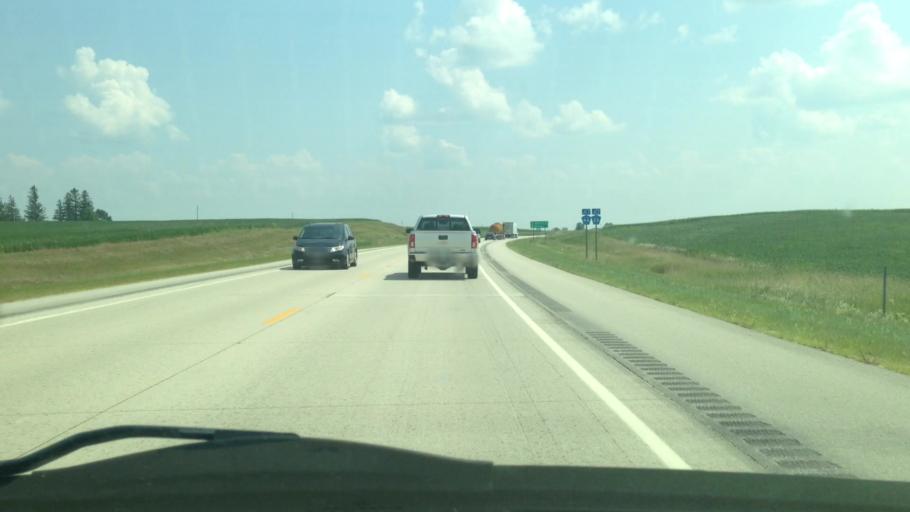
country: US
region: Minnesota
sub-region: Fillmore County
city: Spring Valley
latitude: 43.5466
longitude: -92.3733
